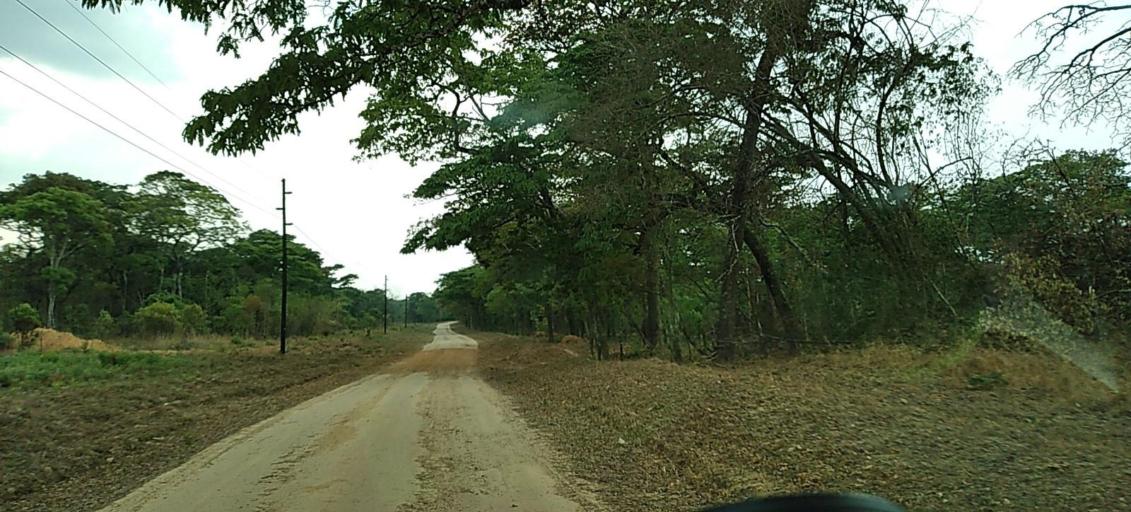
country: ZM
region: North-Western
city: Solwezi
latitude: -12.7688
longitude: 26.4650
